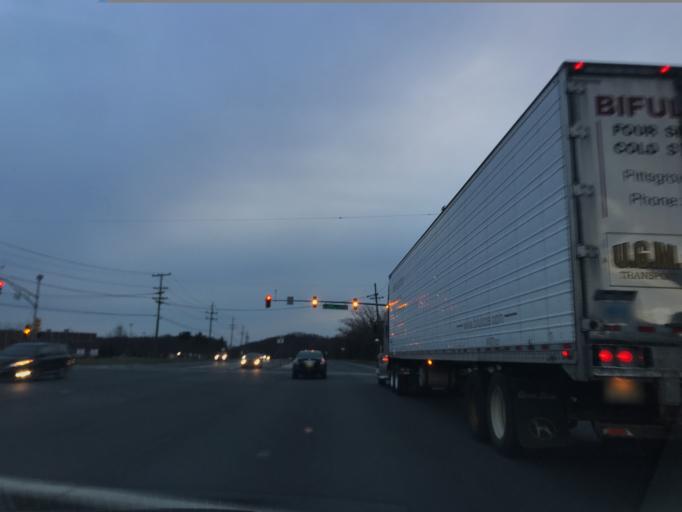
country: US
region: New Jersey
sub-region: Middlesex County
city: Dayton
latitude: 40.4017
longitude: -74.5085
